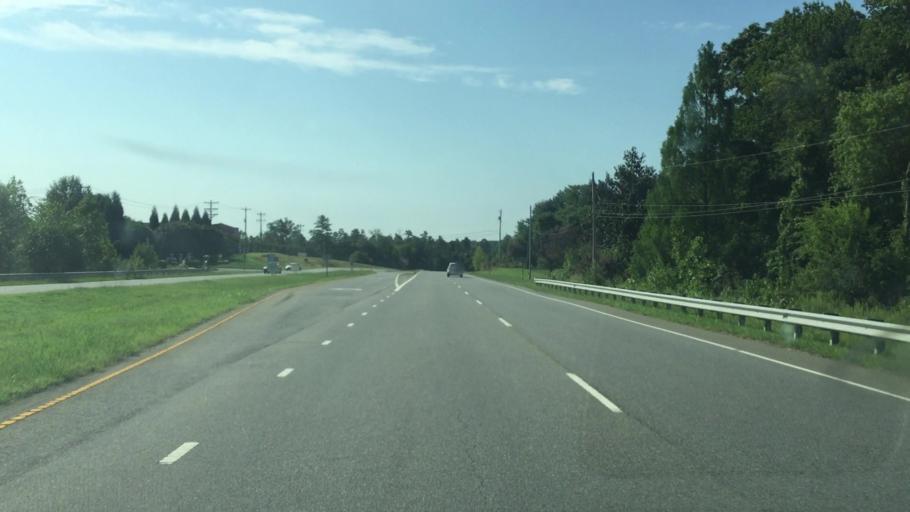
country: US
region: North Carolina
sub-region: Cabarrus County
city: Kannapolis
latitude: 35.4631
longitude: -80.6662
